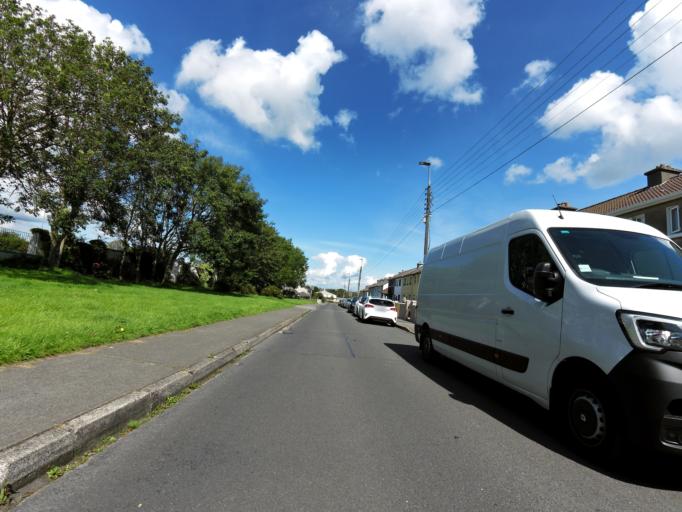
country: IE
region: Connaught
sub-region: County Galway
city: Gaillimh
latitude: 53.2737
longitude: -9.0707
